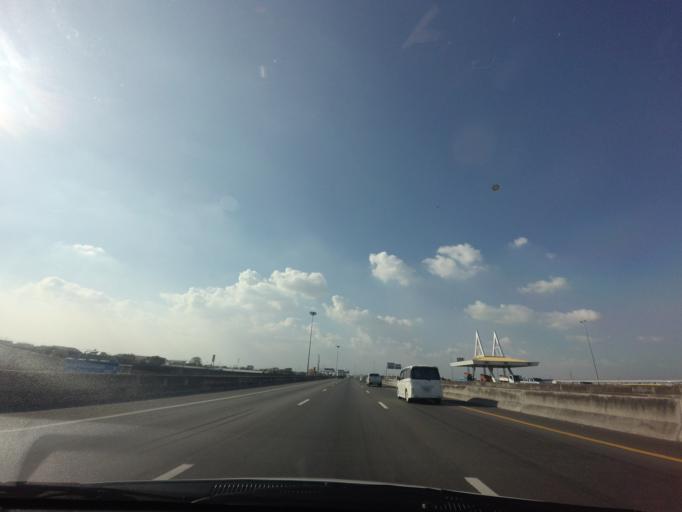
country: TH
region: Samut Prakan
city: Samut Prakan
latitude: 13.6154
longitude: 100.6166
